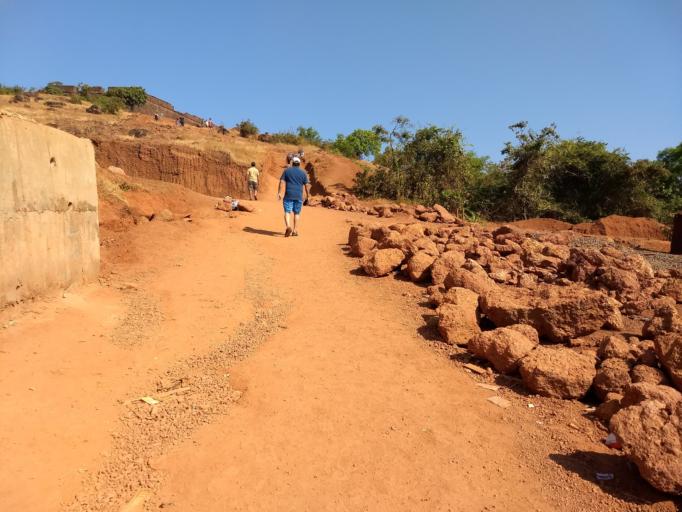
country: IN
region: Goa
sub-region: North Goa
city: Vagator
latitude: 15.6041
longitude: 73.7370
